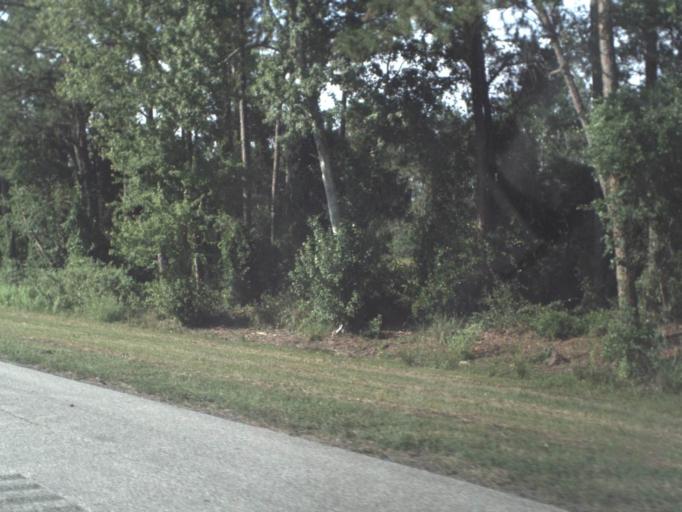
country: US
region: Florida
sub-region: Saint Johns County
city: Saint Augustine Shores
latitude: 29.7783
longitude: -81.3585
